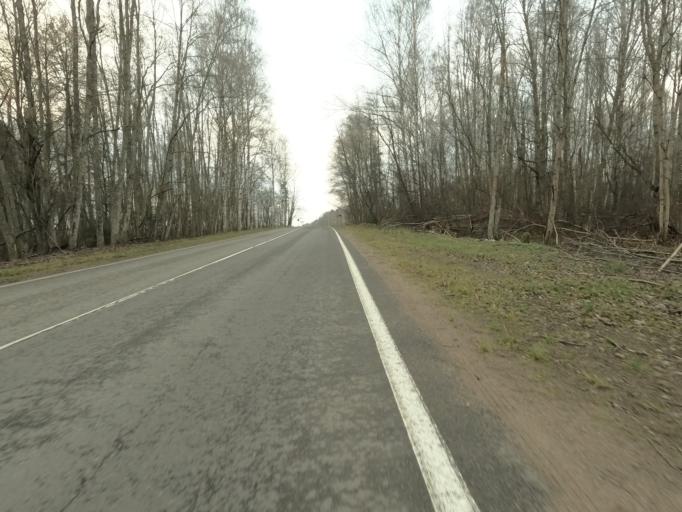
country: RU
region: Leningrad
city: Mga
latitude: 59.7949
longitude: 31.0064
